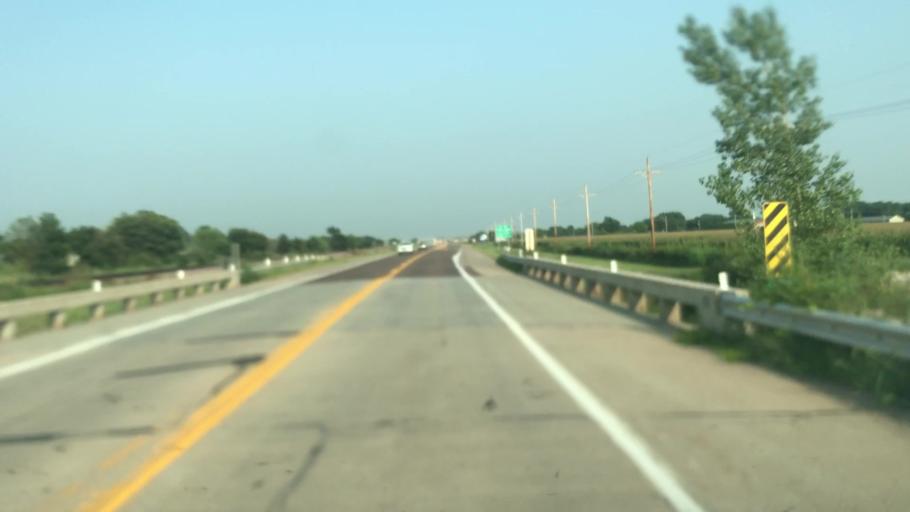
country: US
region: Nebraska
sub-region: Hall County
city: Grand Island
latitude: 40.9598
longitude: -98.4128
